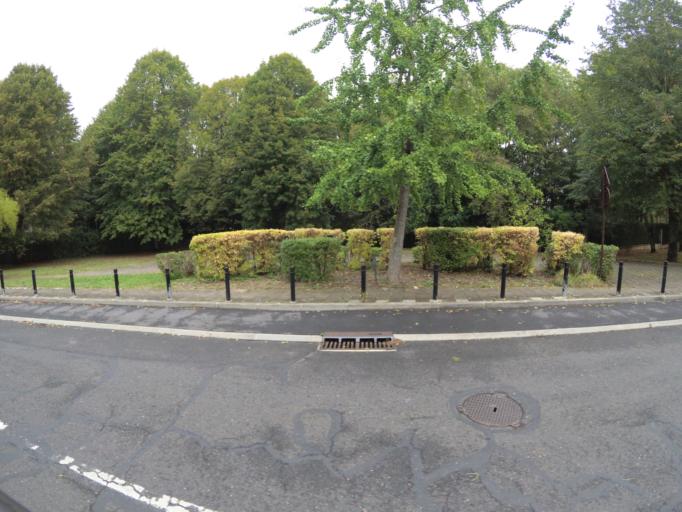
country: FR
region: Ile-de-France
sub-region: Departement de Seine-et-Marne
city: Bussy-Saint-Georges
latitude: 48.8438
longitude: 2.7142
